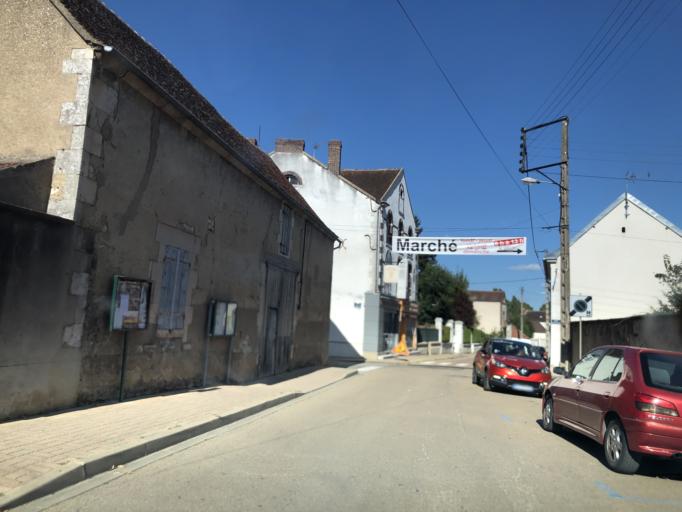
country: FR
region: Bourgogne
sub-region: Departement de l'Yonne
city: Appoigny
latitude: 47.8760
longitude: 3.5273
